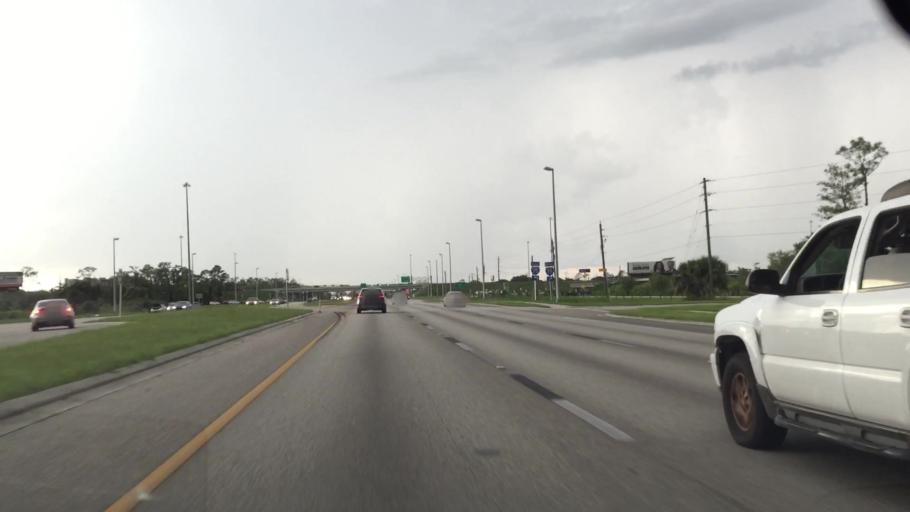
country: US
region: Florida
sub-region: Lee County
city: Fort Myers
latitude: 26.6327
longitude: -81.7977
